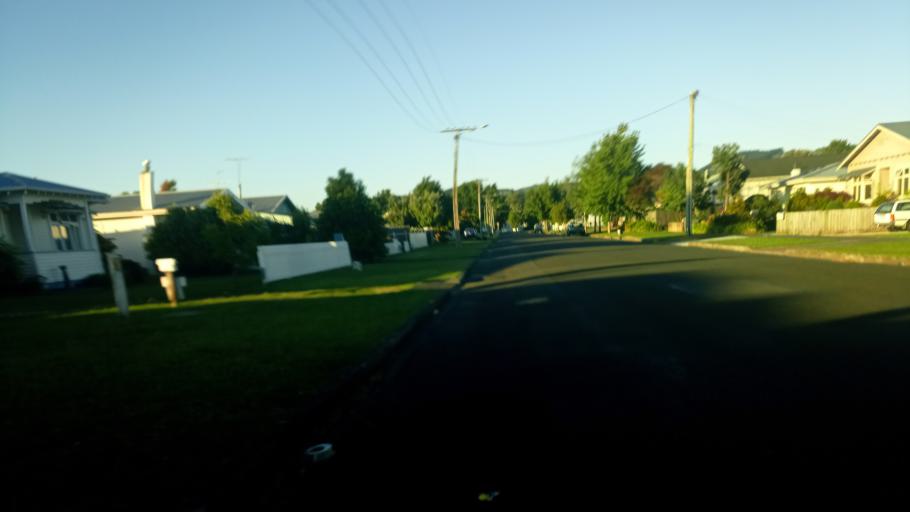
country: NZ
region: Gisborne
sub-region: Gisborne District
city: Gisborne
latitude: -38.6526
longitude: 178.0050
